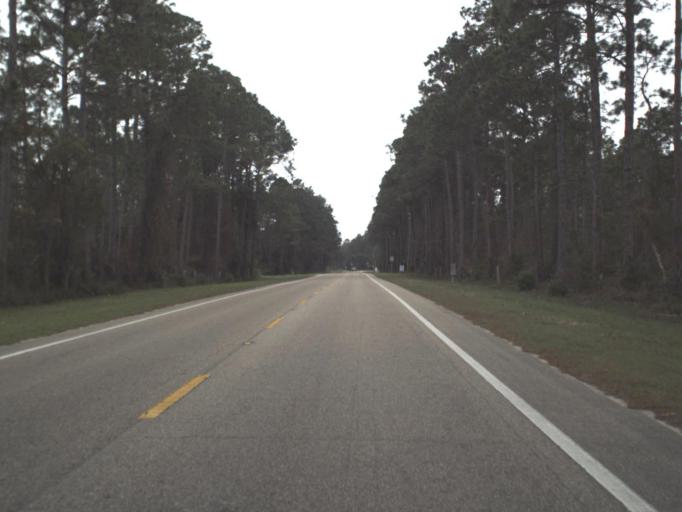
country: US
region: Florida
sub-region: Gulf County
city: Port Saint Joe
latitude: 29.8233
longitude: -85.2815
